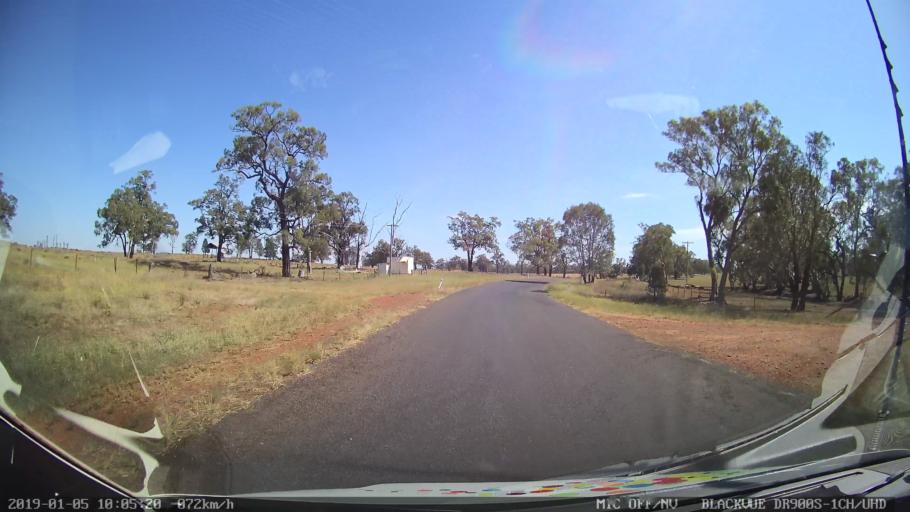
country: AU
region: New South Wales
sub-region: Gilgandra
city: Gilgandra
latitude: -31.6668
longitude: 148.8653
